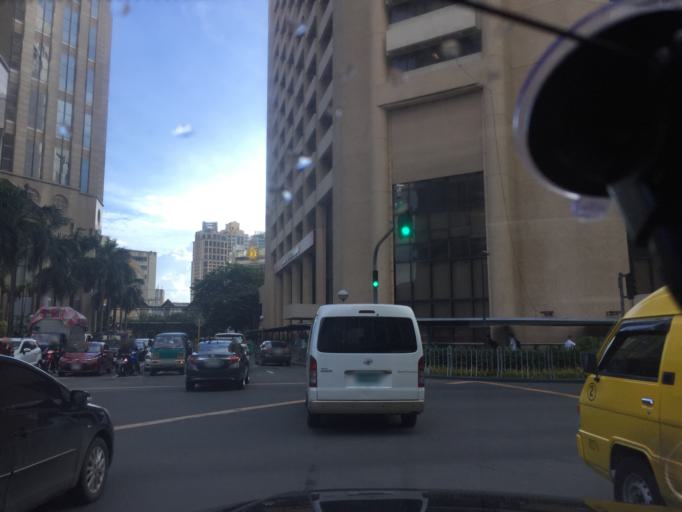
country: PH
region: Metro Manila
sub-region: Makati City
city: Makati City
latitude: 14.5569
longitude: 121.0212
